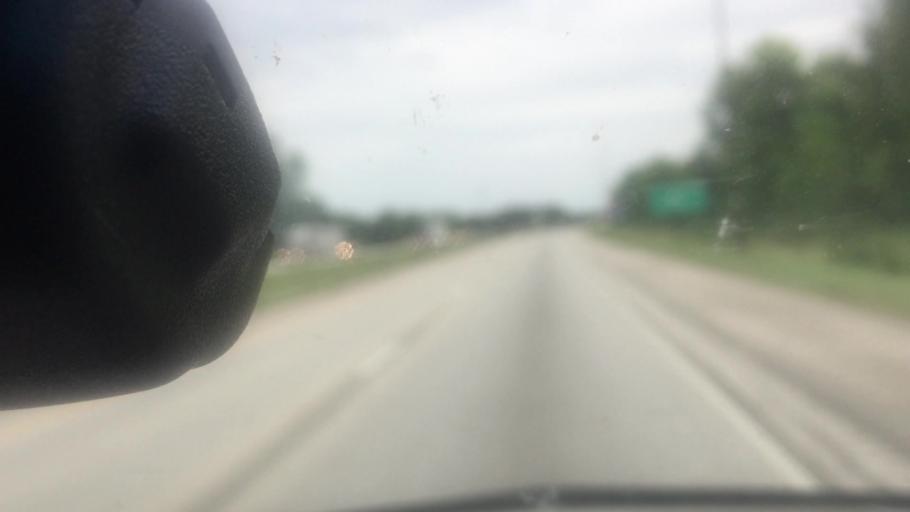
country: US
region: Illinois
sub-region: Sangamon County
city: Grandview
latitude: 39.8122
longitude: -89.5932
